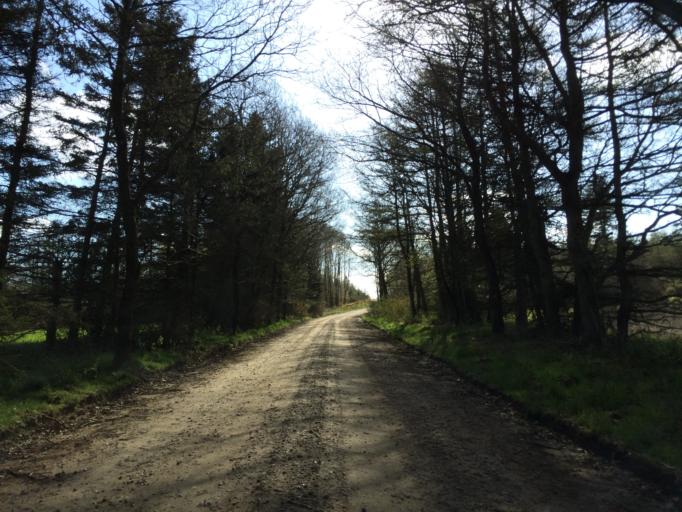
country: DK
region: Central Jutland
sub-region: Holstebro Kommune
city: Ulfborg
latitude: 56.2374
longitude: 8.4723
